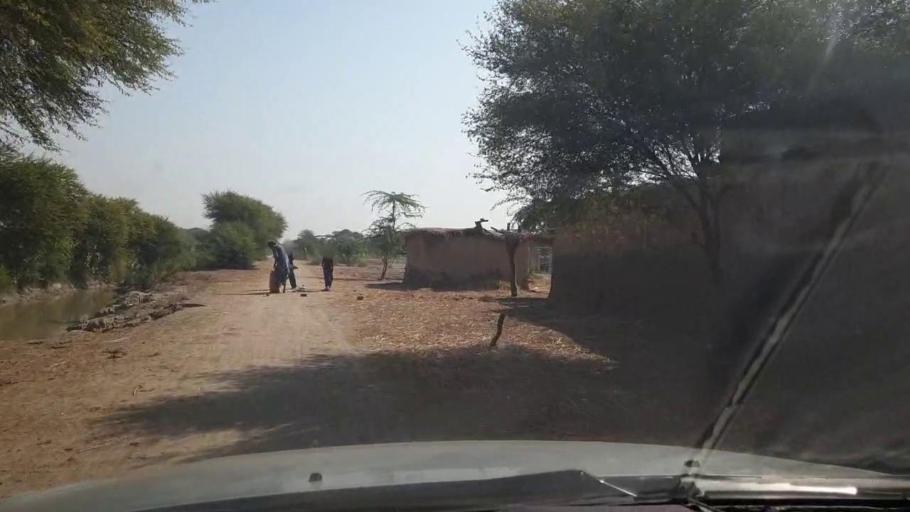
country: PK
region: Sindh
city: Bulri
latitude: 24.9120
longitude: 68.4519
